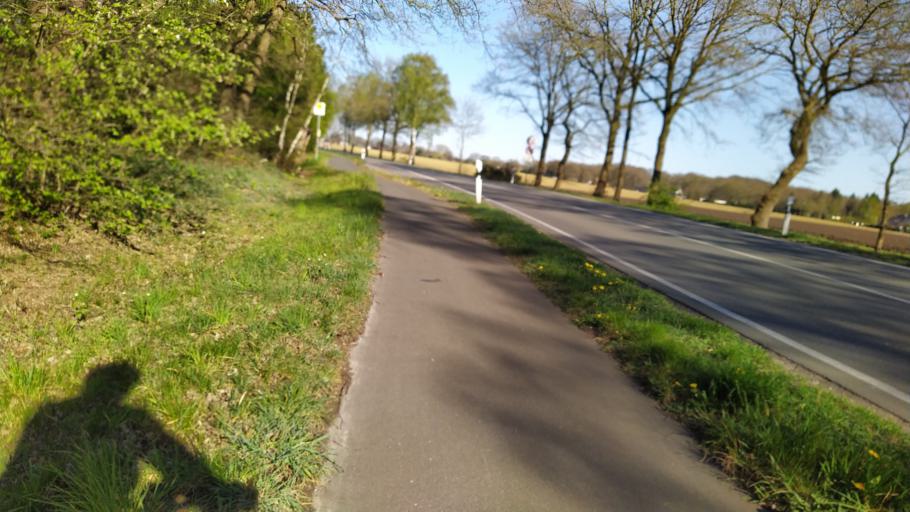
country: DE
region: Lower Saxony
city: Hamersen
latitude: 53.2799
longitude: 9.4800
